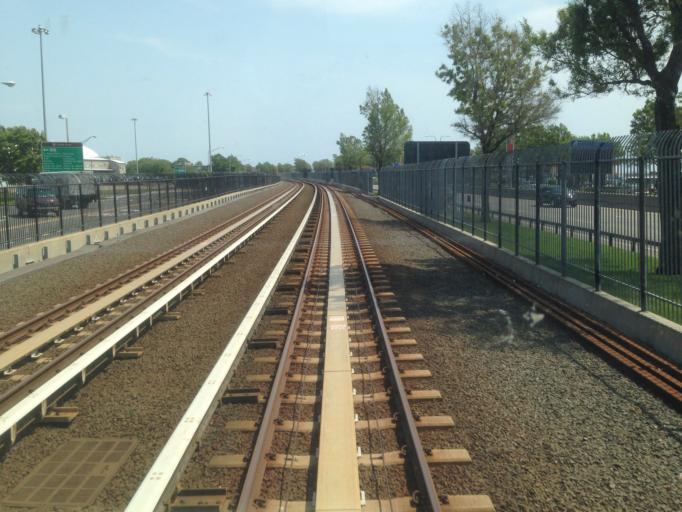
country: US
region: New York
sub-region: Queens County
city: Jamaica
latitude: 40.6495
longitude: -73.8039
